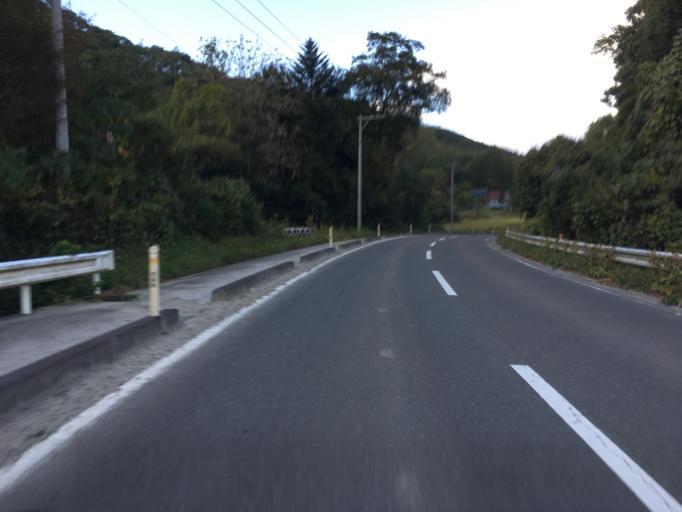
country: JP
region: Miyagi
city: Marumori
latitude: 37.8386
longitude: 140.8295
